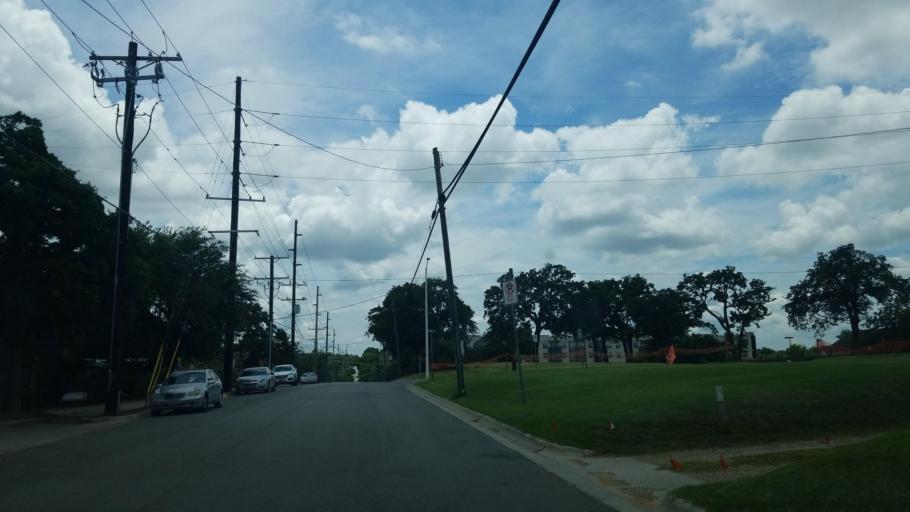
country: US
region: Texas
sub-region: Denton County
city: Denton
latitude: 33.2087
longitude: -97.1416
